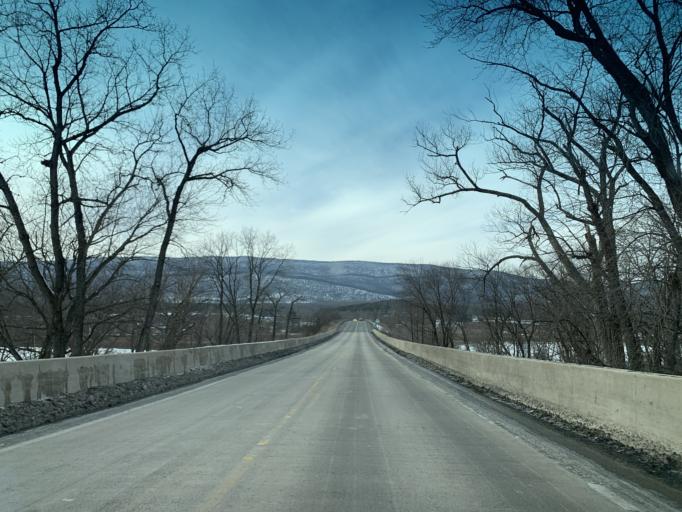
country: US
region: Maryland
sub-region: Allegany County
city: Bel Air
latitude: 39.5621
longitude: -78.8474
